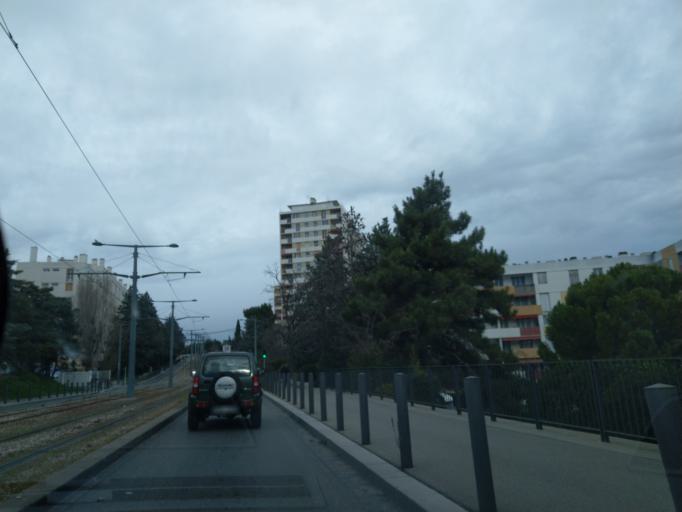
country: FR
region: Provence-Alpes-Cote d'Azur
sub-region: Departement des Bouches-du-Rhone
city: Marseille 12
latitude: 43.2928
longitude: 5.4350
